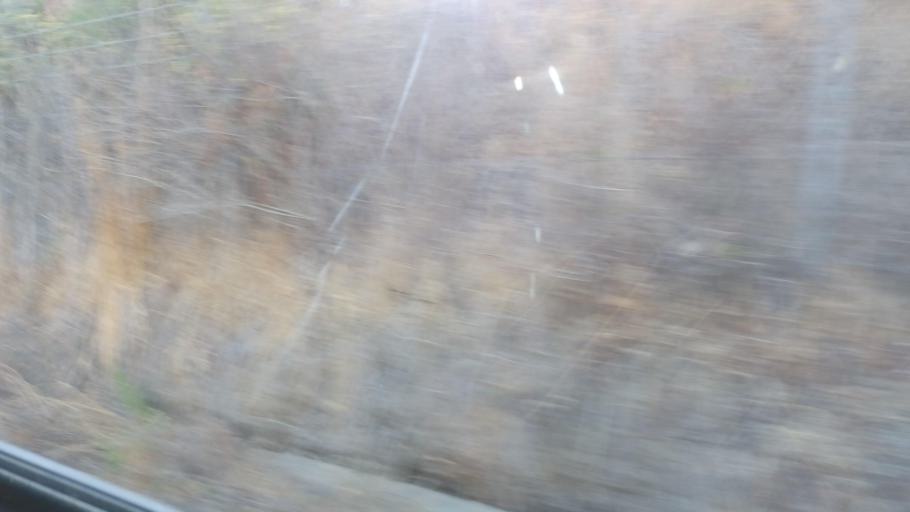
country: CY
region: Pafos
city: Tala
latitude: 34.9280
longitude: 32.4855
